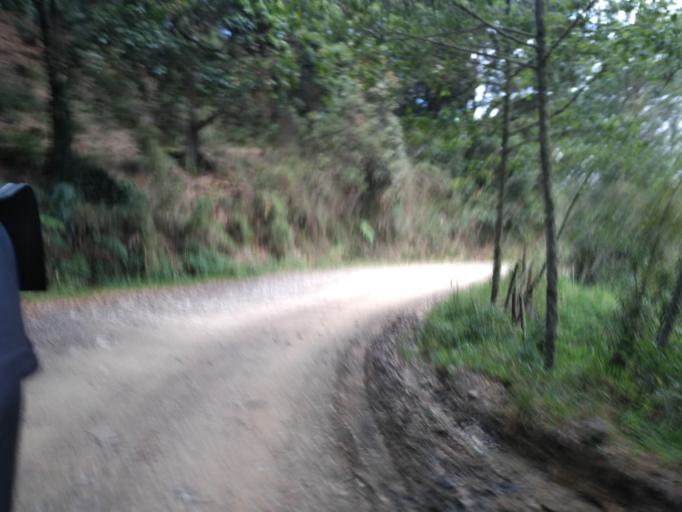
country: CO
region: Boyaca
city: Duitama
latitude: 5.9436
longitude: -73.1322
